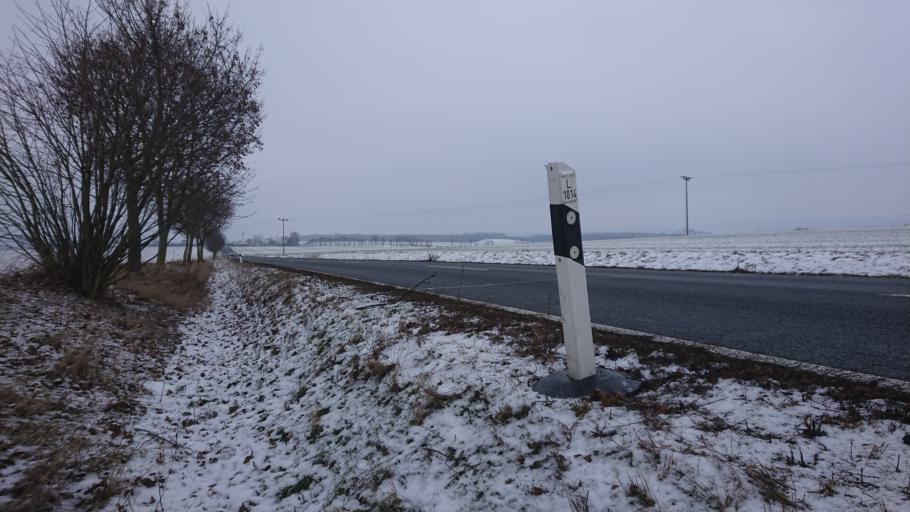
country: DE
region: Thuringia
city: Breitenworbis
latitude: 51.3976
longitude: 10.4135
